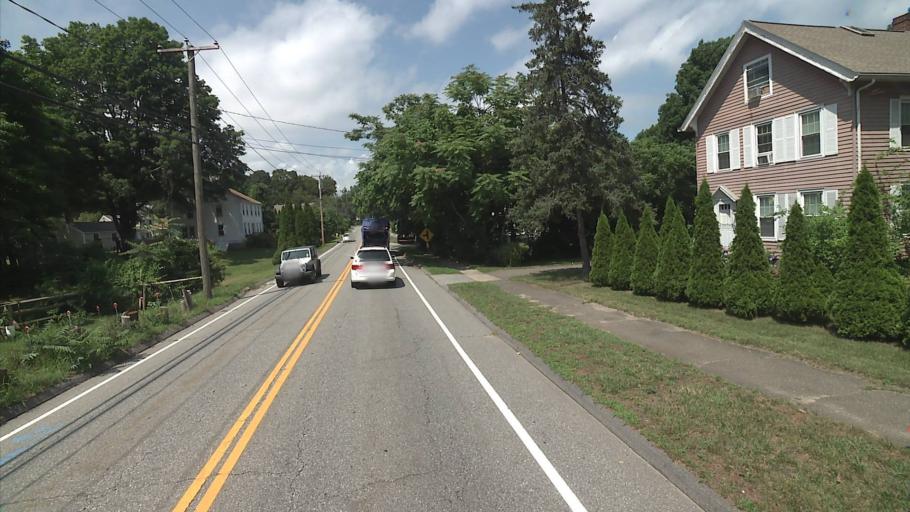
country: US
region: Connecticut
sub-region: Middlesex County
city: Clinton
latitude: 41.2819
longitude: -72.5267
